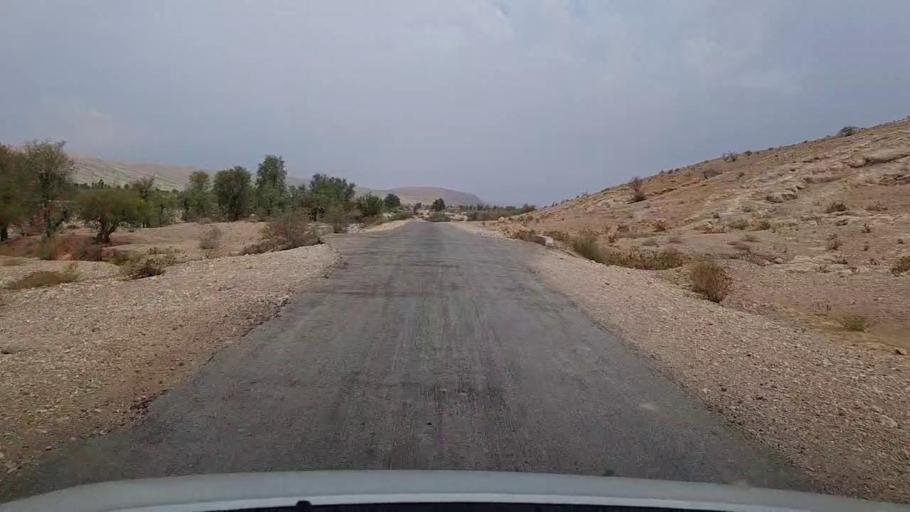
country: PK
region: Sindh
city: Sehwan
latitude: 26.2217
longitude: 67.7138
